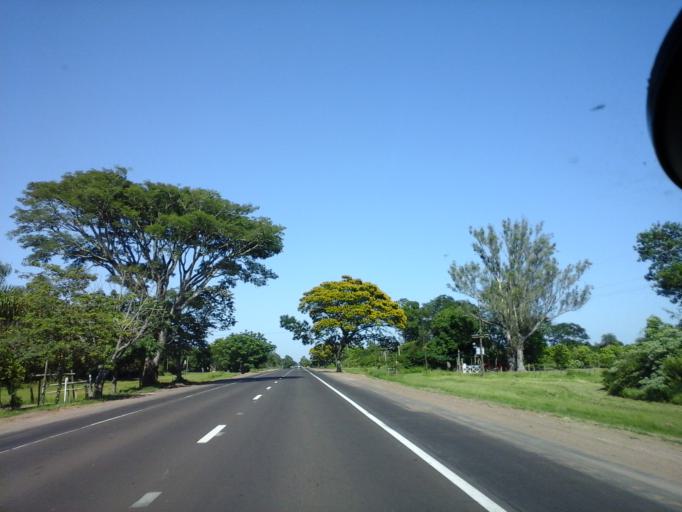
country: AR
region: Corrientes
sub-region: Departamento de Itati
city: Itati
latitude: -27.3664
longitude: -58.3230
